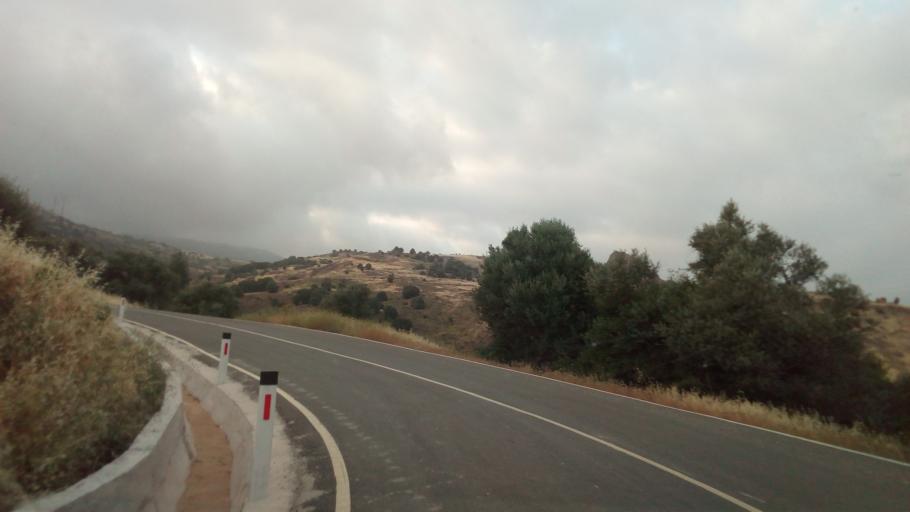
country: CY
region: Limassol
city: Pachna
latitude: 34.8512
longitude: 32.6541
